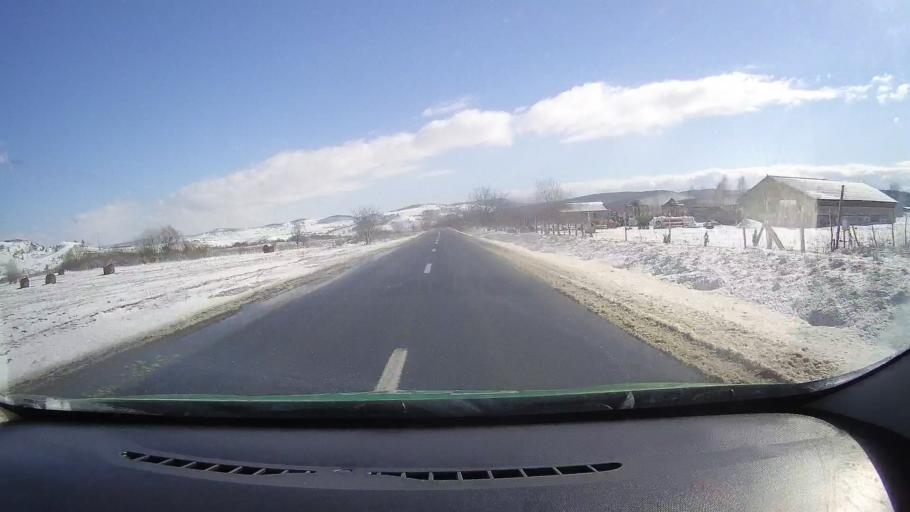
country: RO
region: Sibiu
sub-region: Comuna Rosia
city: Rosia
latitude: 45.7928
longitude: 24.2943
